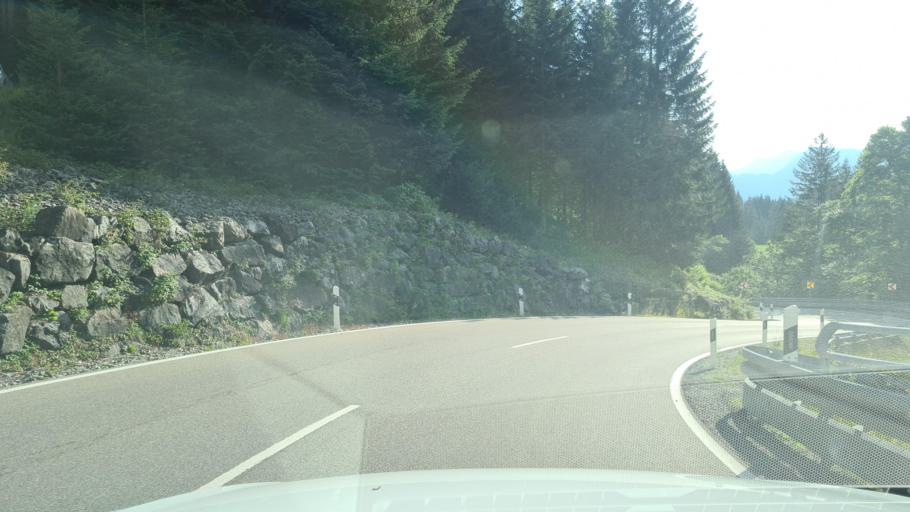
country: DE
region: Bavaria
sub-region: Swabia
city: Obermaiselstein
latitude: 47.4340
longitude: 10.1881
